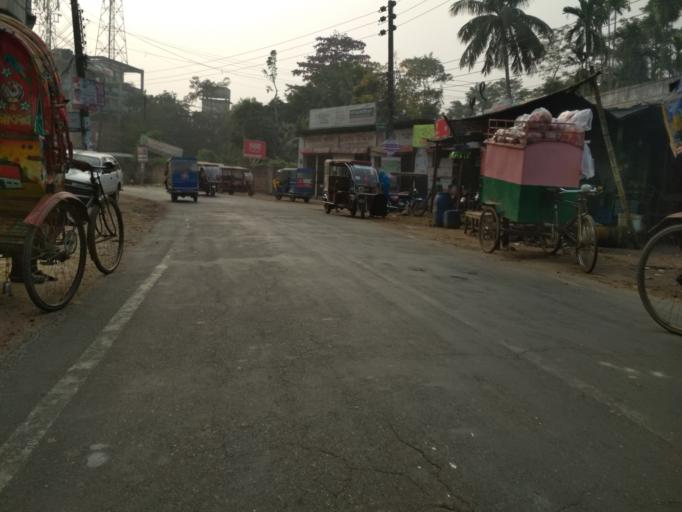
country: BD
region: Chittagong
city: Lakshmipur
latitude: 22.9361
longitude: 90.8388
